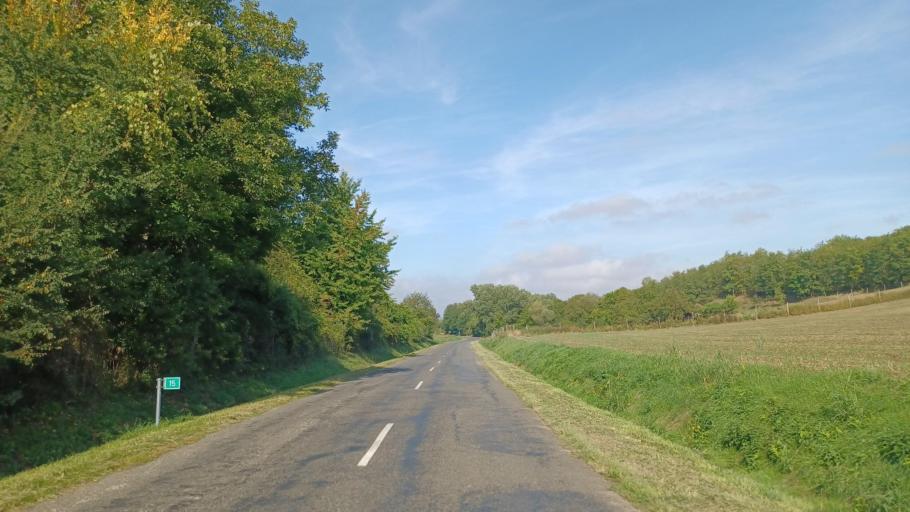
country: HU
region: Tolna
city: Pincehely
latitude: 46.6894
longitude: 18.4588
